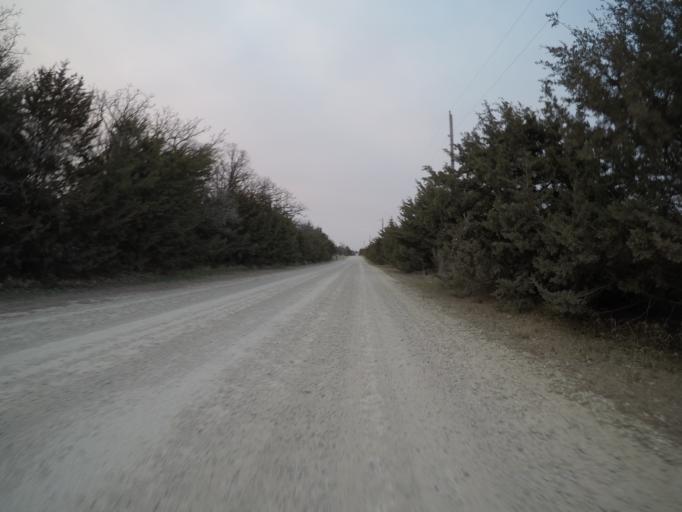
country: US
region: Kansas
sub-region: Riley County
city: Manhattan
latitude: 39.2409
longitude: -96.6537
